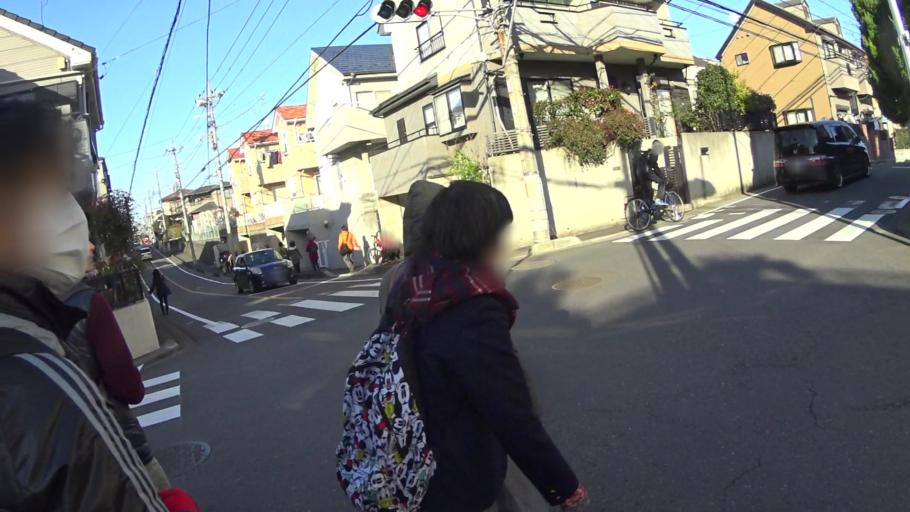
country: JP
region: Saitama
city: Yono
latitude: 35.8582
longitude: 139.6395
